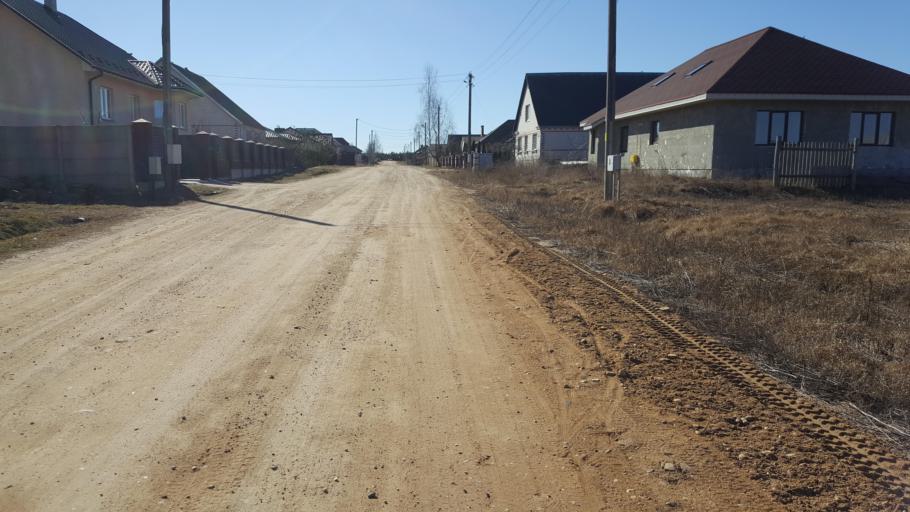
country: BY
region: Brest
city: Kamyanyets
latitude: 52.4000
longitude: 23.8448
